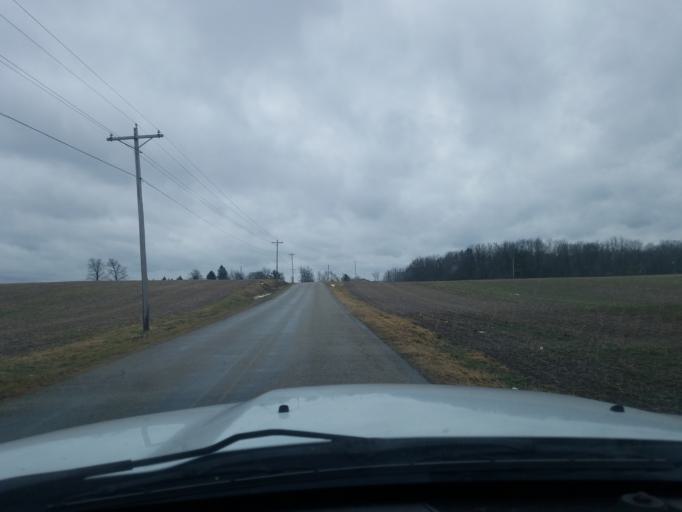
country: US
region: Indiana
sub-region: Noble County
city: Albion
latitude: 41.4269
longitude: -85.3955
